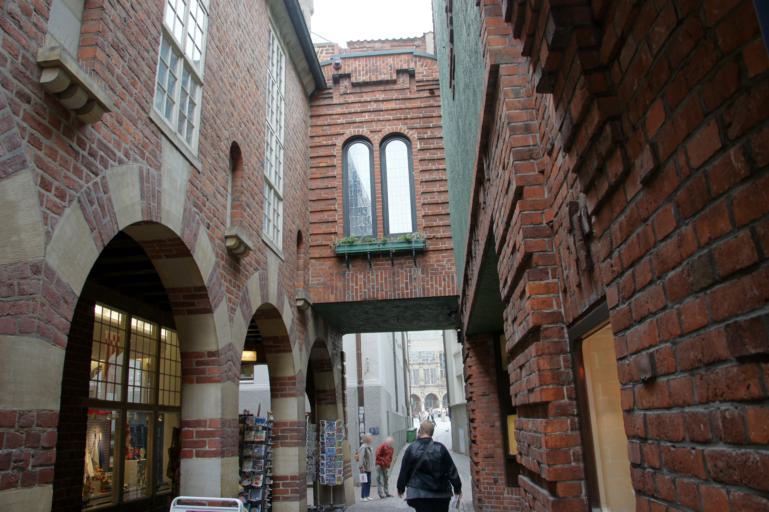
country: DE
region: Bremen
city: Bremen
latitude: 53.0754
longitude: 8.8061
